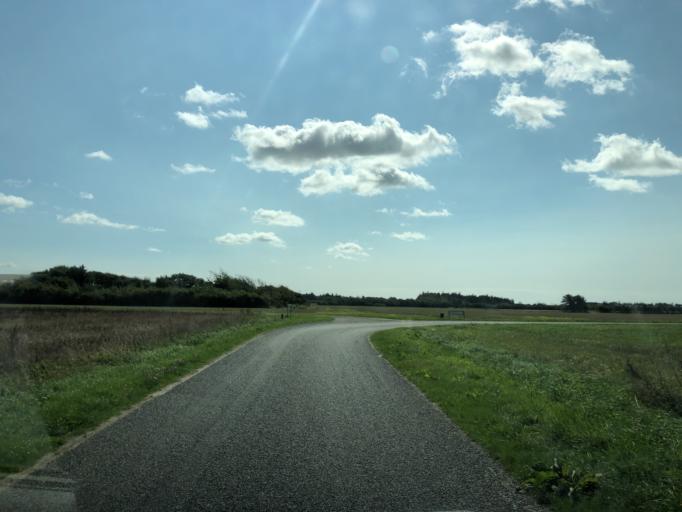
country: DK
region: Central Jutland
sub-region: Holstebro Kommune
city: Ulfborg
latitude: 56.2613
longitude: 8.1689
